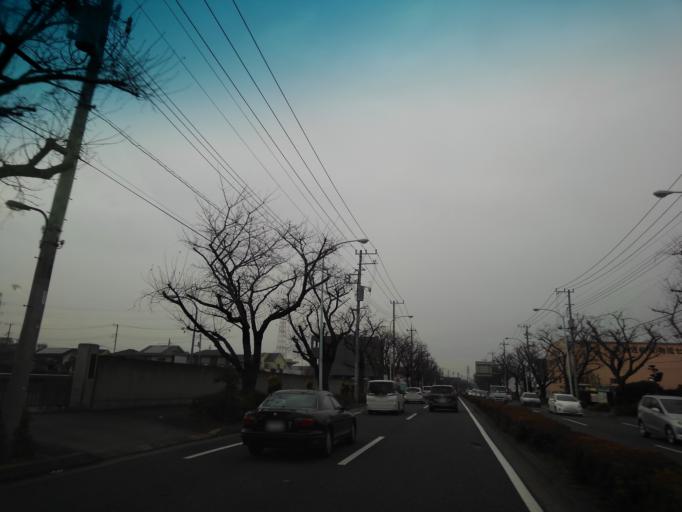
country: JP
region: Tokyo
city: Kokubunji
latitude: 35.6752
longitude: 139.4590
